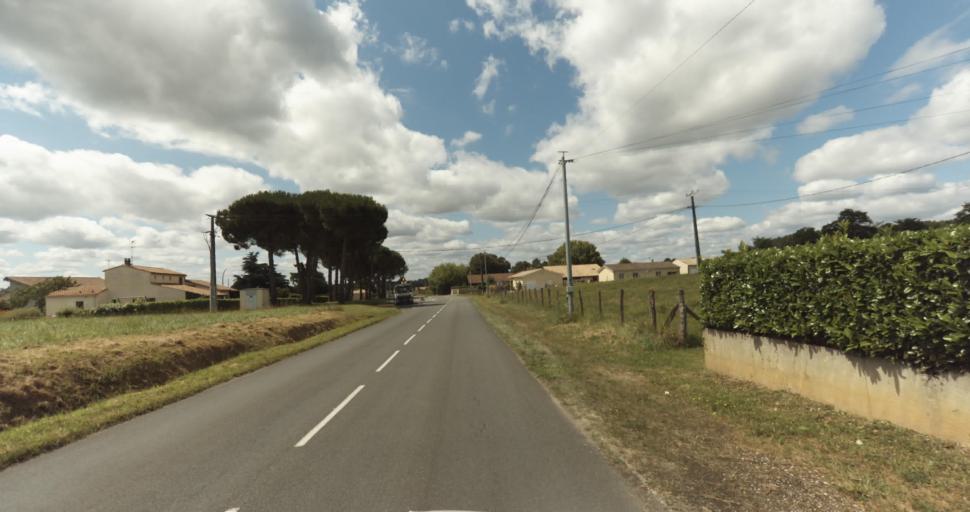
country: FR
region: Aquitaine
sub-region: Departement de la Gironde
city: Bazas
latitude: 44.4401
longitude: -0.2069
